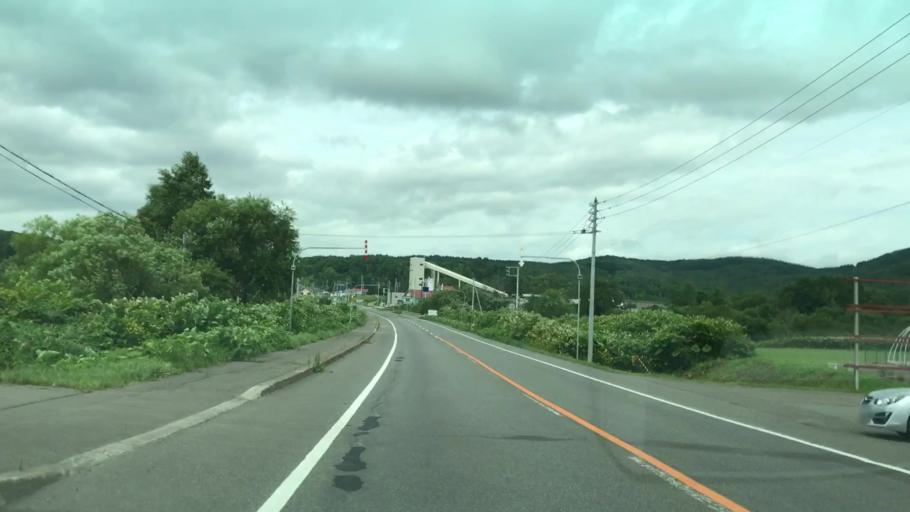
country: JP
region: Hokkaido
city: Niseko Town
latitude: 42.9184
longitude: 140.7454
